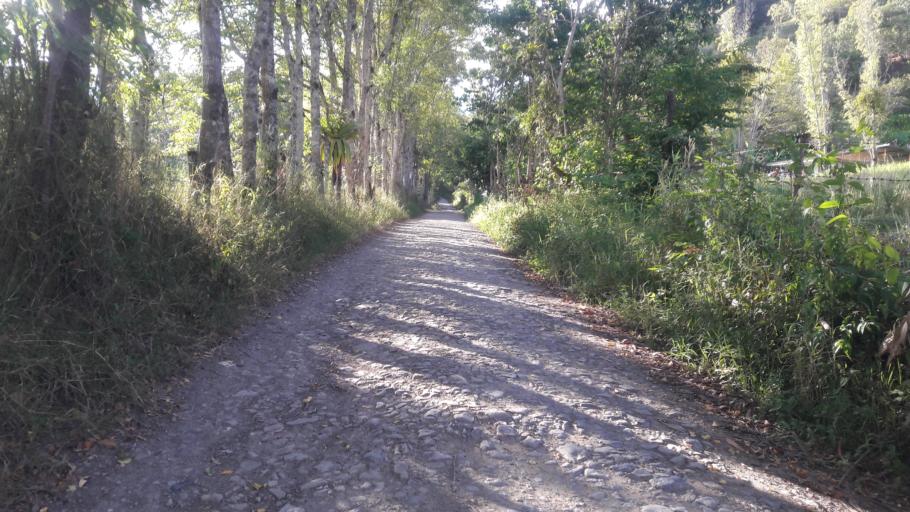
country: CO
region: Cundinamarca
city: Tenza
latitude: 5.0885
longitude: -73.4250
